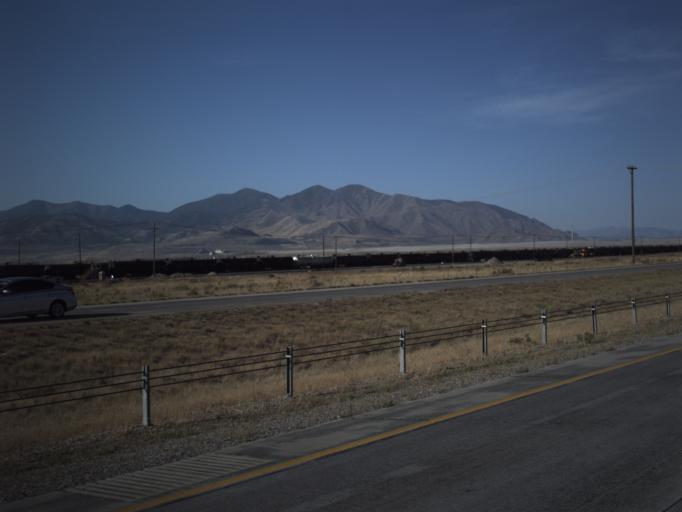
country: US
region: Utah
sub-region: Salt Lake County
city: Magna
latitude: 40.7712
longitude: -112.0476
